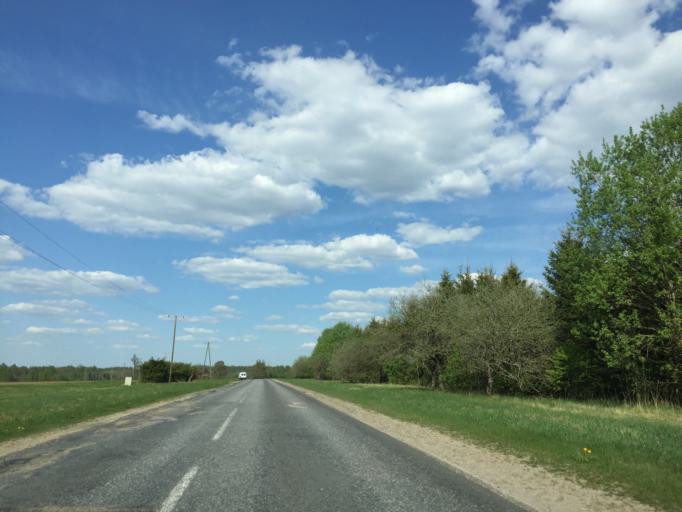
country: LV
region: Limbazu Rajons
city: Limbazi
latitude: 57.4296
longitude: 24.7122
